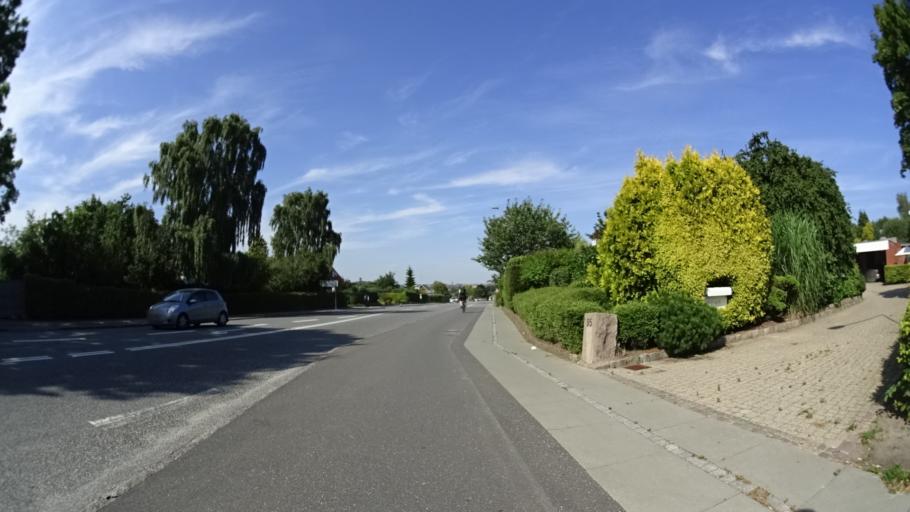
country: DK
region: Central Jutland
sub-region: Arhus Kommune
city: Arhus
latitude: 56.1250
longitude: 10.1717
